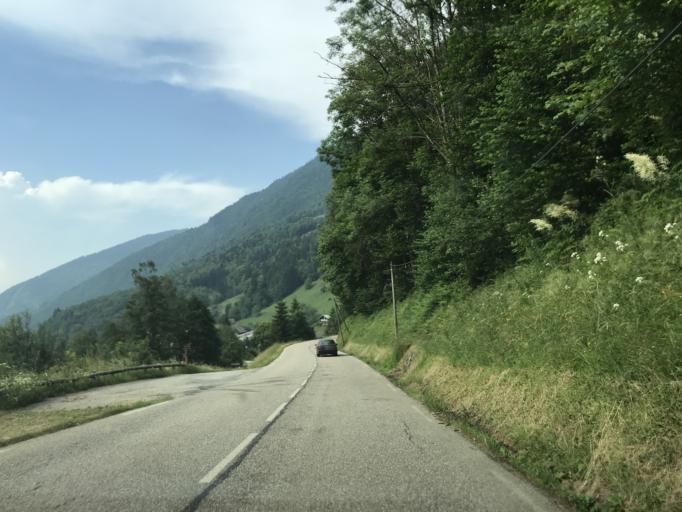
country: FR
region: Rhone-Alpes
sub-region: Departement de l'Isere
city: Allevard
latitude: 45.3516
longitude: 6.0988
